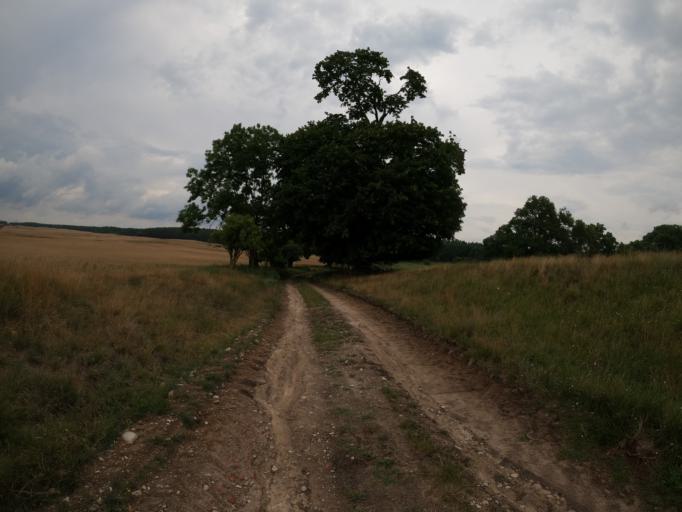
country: DE
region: Brandenburg
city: Althuttendorf
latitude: 53.0283
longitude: 13.8893
